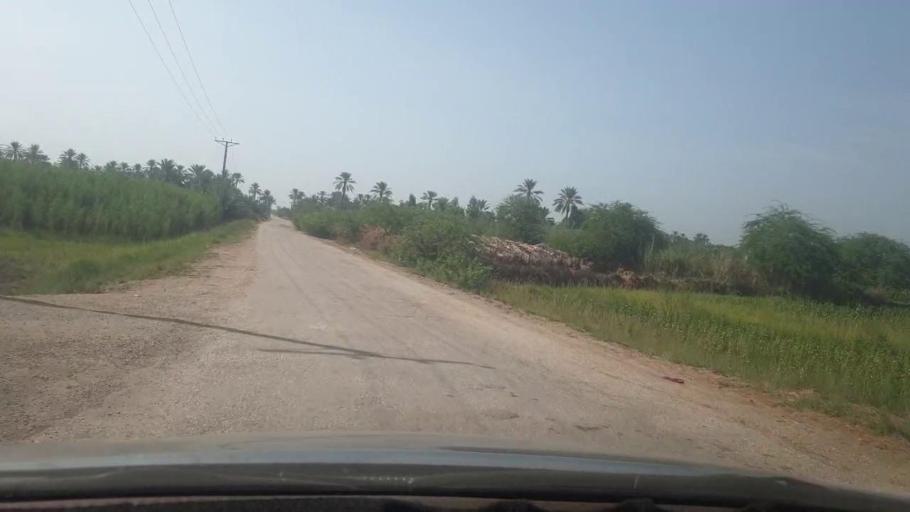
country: PK
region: Sindh
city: Gambat
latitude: 27.3279
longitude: 68.5511
